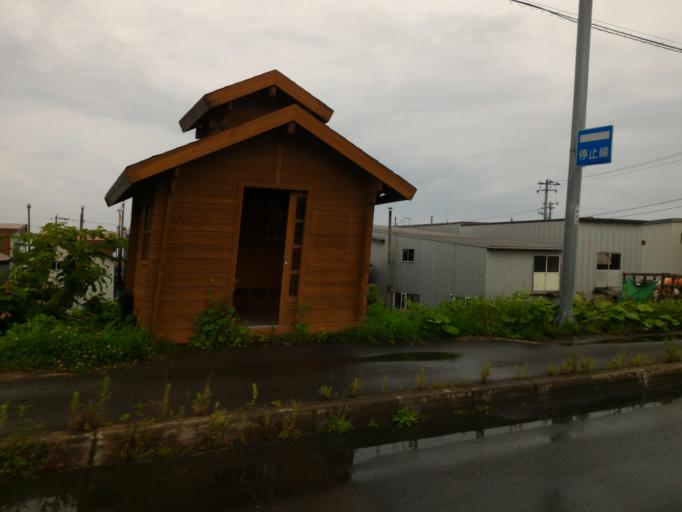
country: JP
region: Hokkaido
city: Rumoi
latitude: 43.9965
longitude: 141.6523
